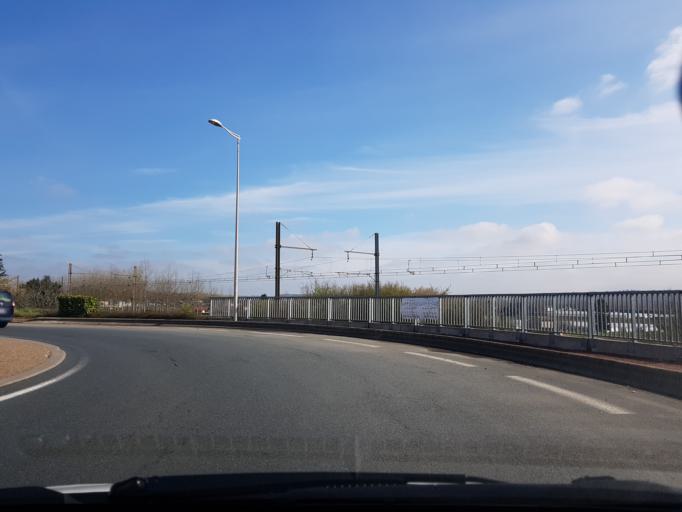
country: FR
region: Rhone-Alpes
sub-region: Departement du Rhone
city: Villefranche-sur-Saone
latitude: 45.9652
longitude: 4.7163
